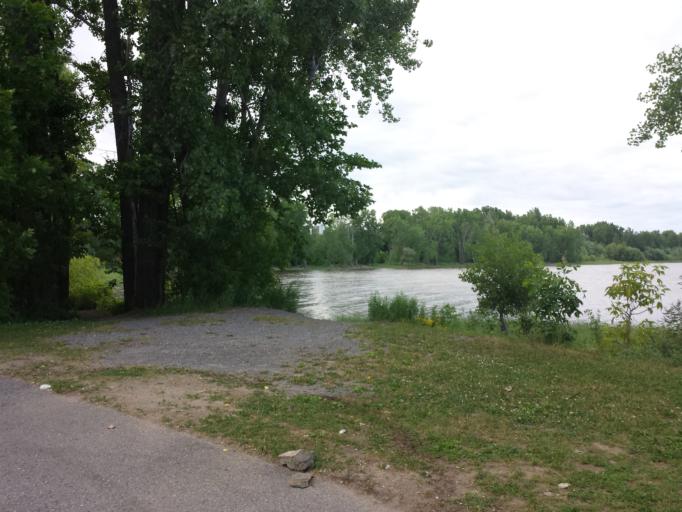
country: CA
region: Ontario
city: Bells Corners
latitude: 45.3644
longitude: -75.8054
